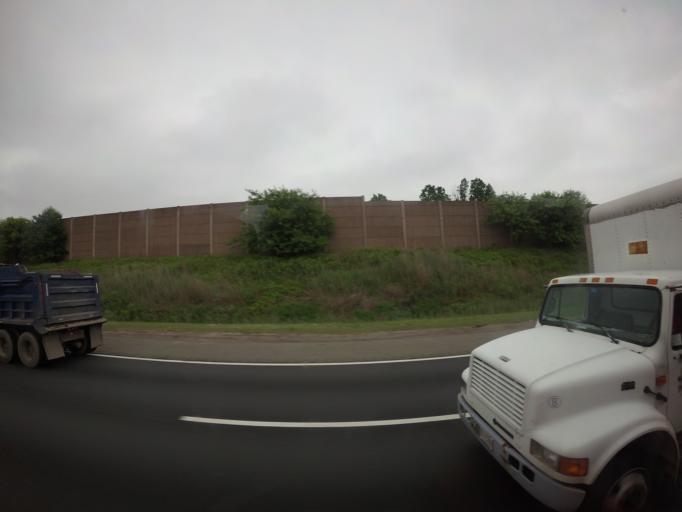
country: US
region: New Jersey
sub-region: Middlesex County
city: Carteret
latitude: 40.5857
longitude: -74.2398
